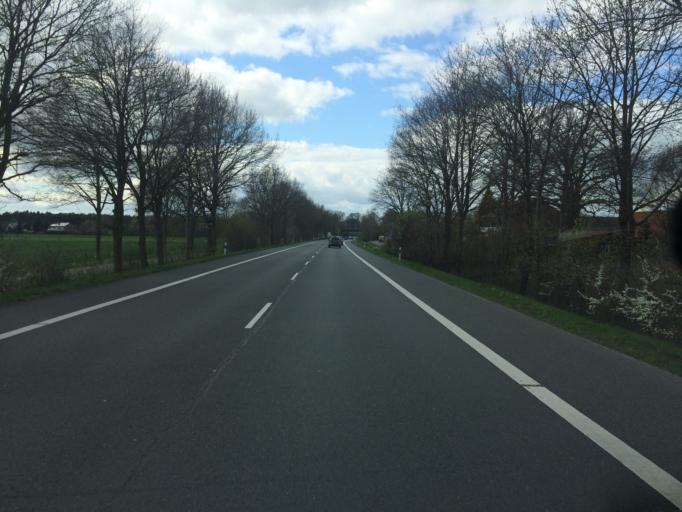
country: DE
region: North Rhine-Westphalia
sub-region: Regierungsbezirk Munster
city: Coesfeld
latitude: 51.9337
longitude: 7.1357
